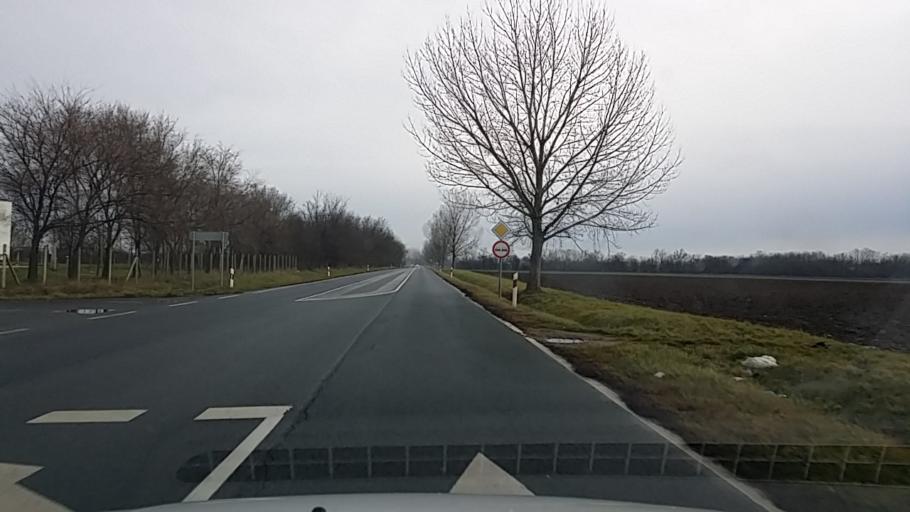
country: HU
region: Vas
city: Celldomolk
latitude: 47.2739
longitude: 17.1720
